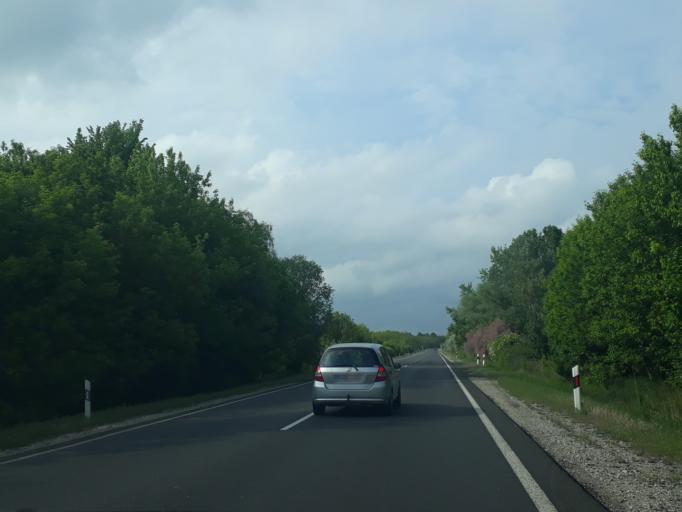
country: HU
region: Szabolcs-Szatmar-Bereg
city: Nyirtass
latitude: 48.0920
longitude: 21.9871
